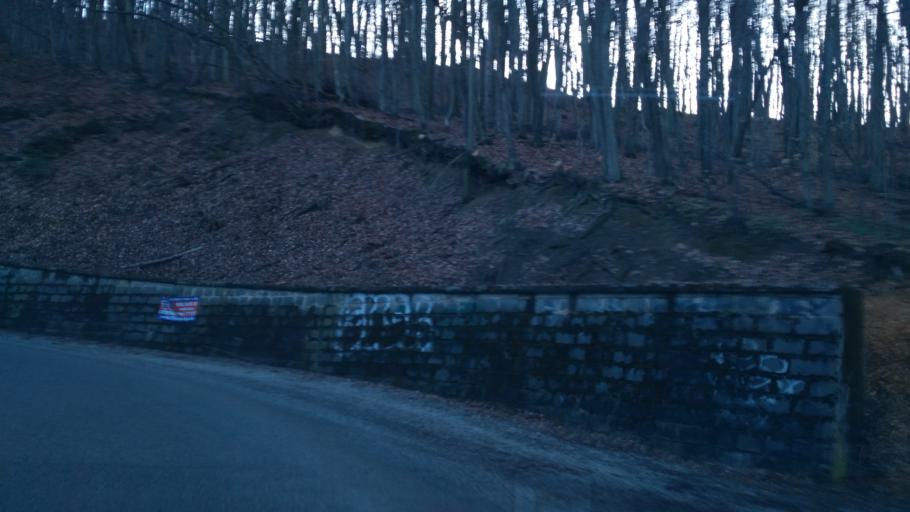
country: SK
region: Kosicky
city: Kosice
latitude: 48.7484
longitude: 21.2037
